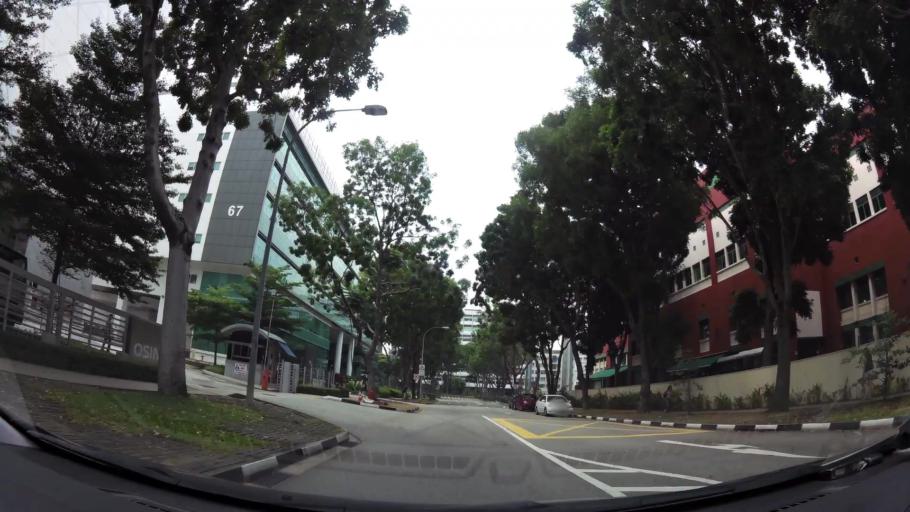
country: SG
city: Singapore
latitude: 1.3248
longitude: 103.8935
